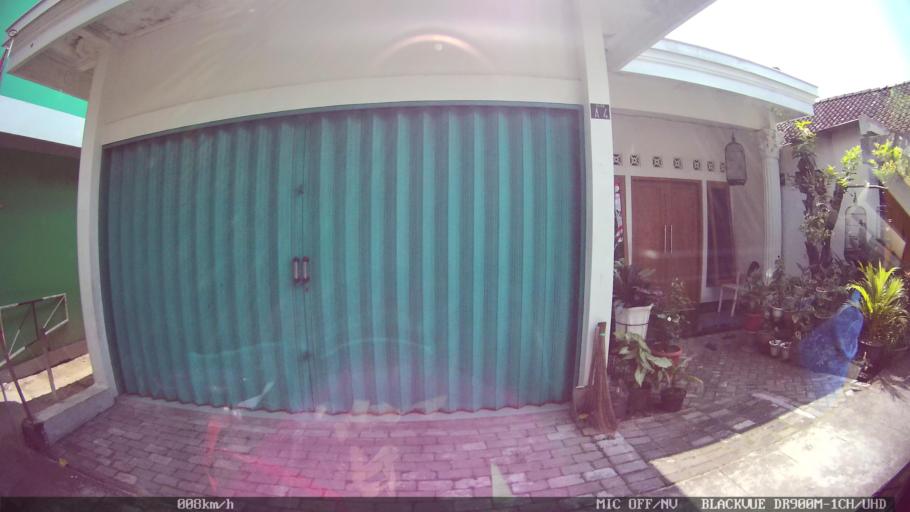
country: ID
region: Daerah Istimewa Yogyakarta
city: Yogyakarta
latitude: -7.7670
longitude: 110.3853
